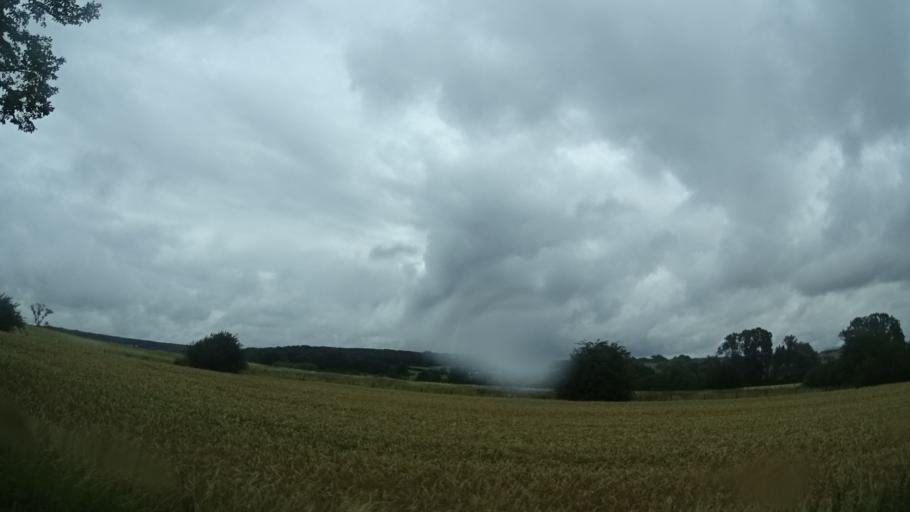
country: LU
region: Luxembourg
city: Bergem
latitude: 49.5200
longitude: 6.0523
